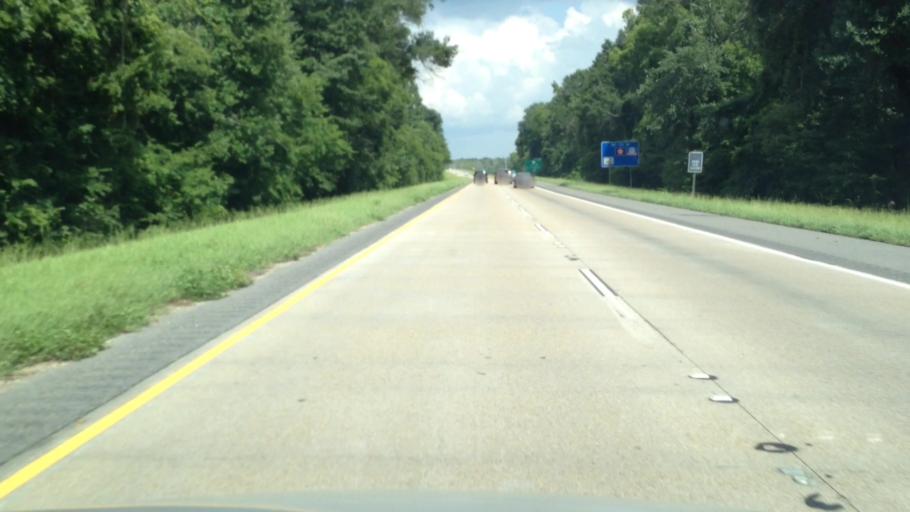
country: US
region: Louisiana
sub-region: Ascension Parish
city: Sorrento
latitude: 30.1754
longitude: -90.8859
